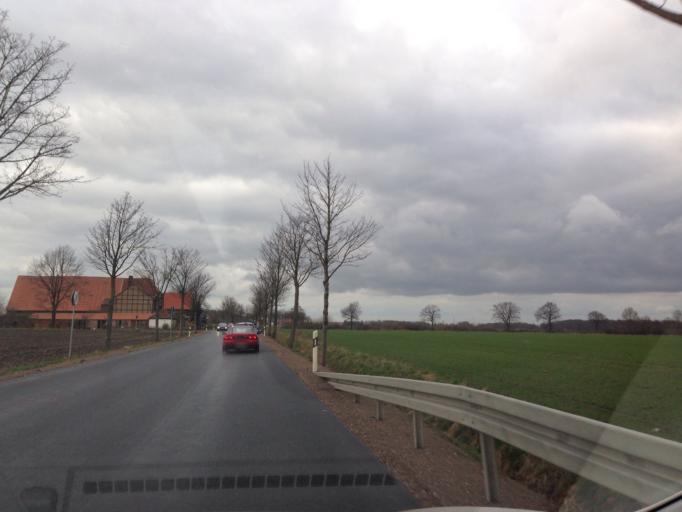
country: DE
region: North Rhine-Westphalia
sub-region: Regierungsbezirk Munster
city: Nordkirchen
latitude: 51.7794
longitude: 7.5450
